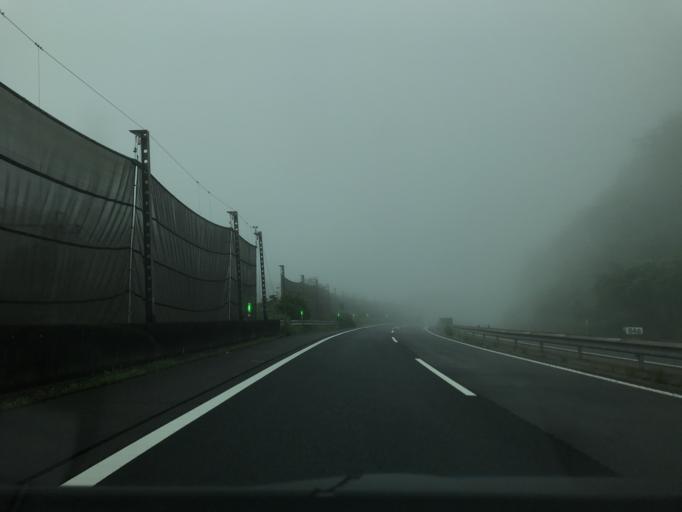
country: JP
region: Oita
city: Hiji
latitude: 33.3597
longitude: 131.4504
